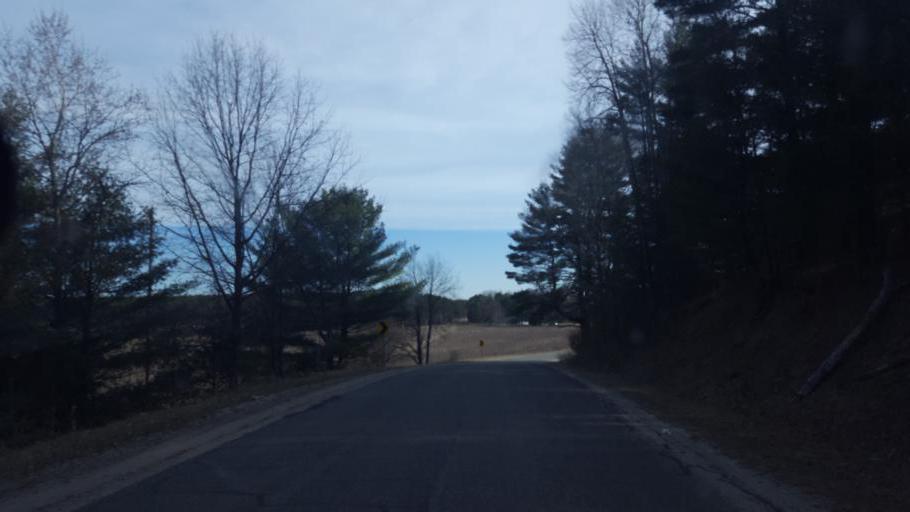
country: US
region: Michigan
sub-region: Mecosta County
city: Big Rapids
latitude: 43.5584
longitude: -85.5277
